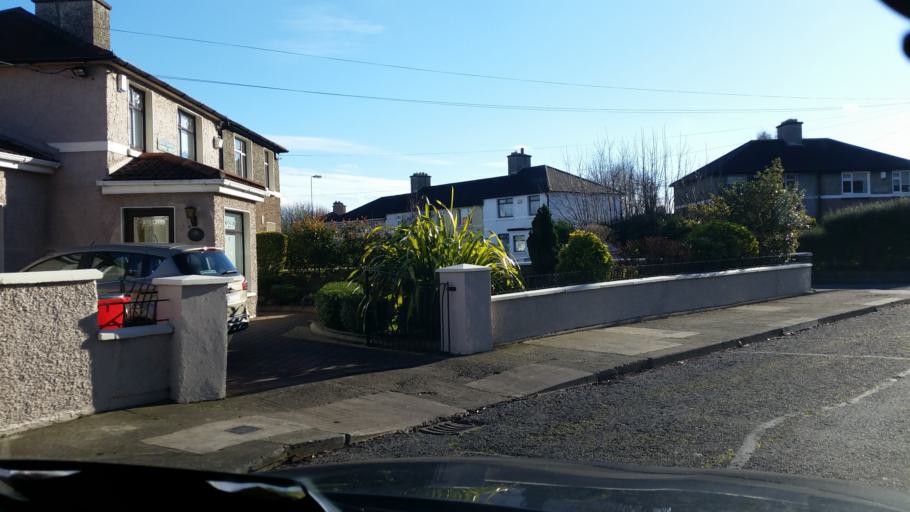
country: IE
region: Leinster
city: Marino
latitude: 53.3673
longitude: -6.2360
